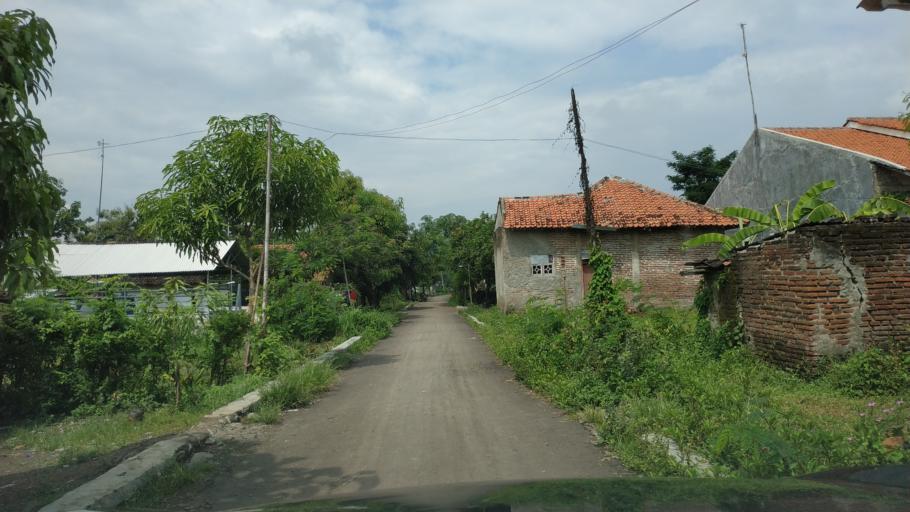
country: ID
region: Central Java
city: Margasari
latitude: -7.0944
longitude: 108.9747
